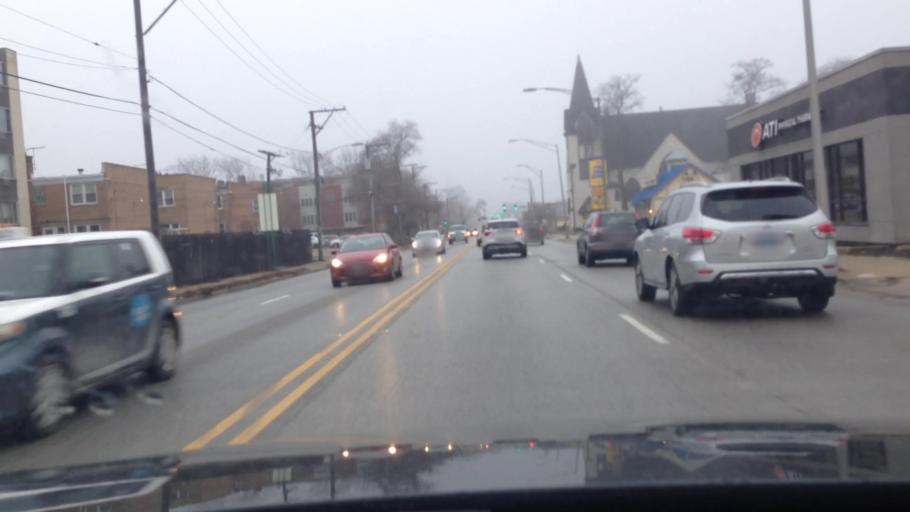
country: US
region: Illinois
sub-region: Cook County
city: Forest Park
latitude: 41.8853
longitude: -87.8049
